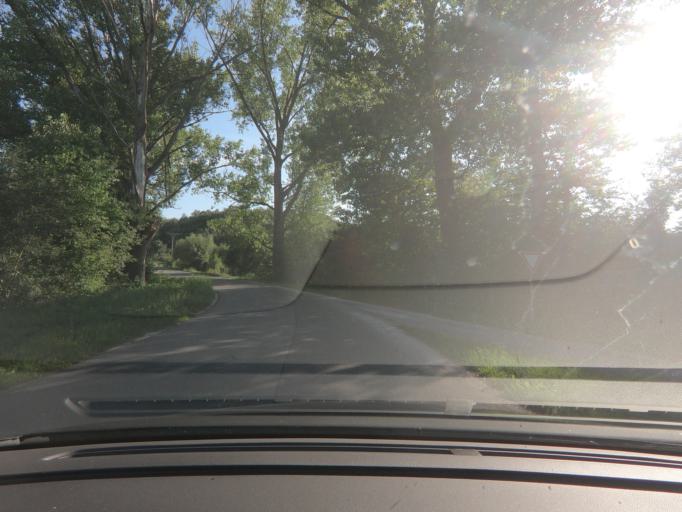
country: SK
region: Nitriansky
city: Stara Tura
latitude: 48.7305
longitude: 17.6856
